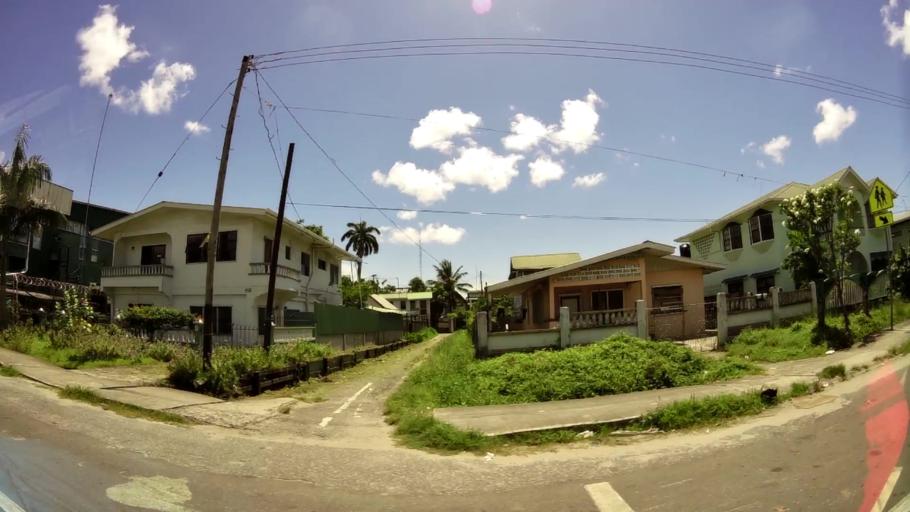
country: GY
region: Demerara-Mahaica
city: Georgetown
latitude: 6.7951
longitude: -58.1690
